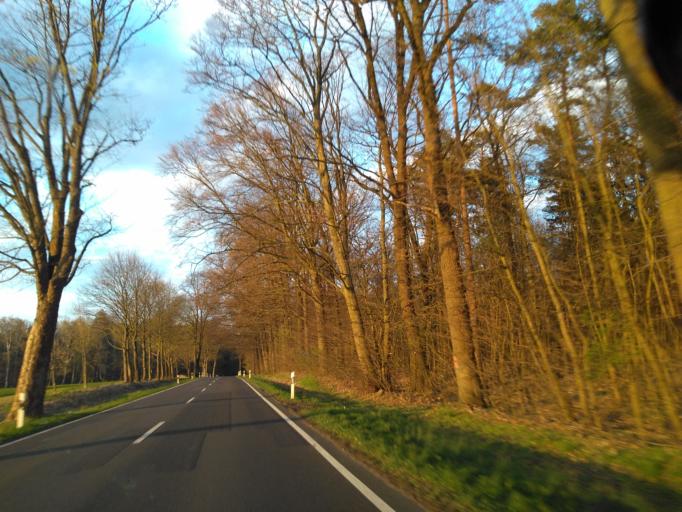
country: DE
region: Brandenburg
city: Protzel
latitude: 52.6284
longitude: 13.9724
